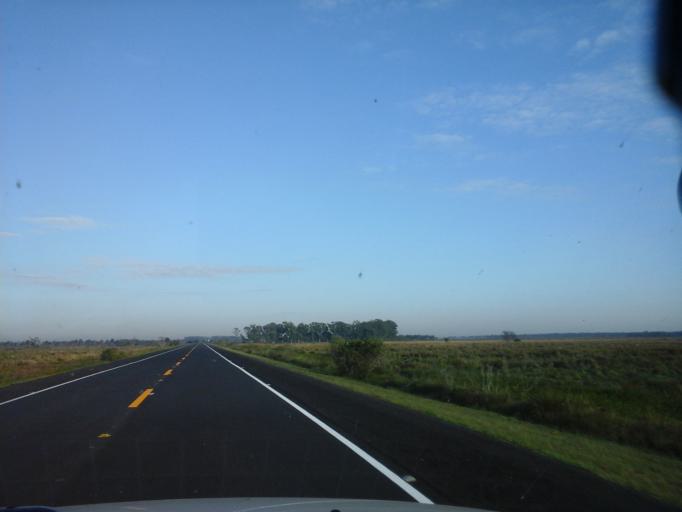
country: PY
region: Neembucu
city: Cerrito
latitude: -26.8683
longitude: -57.7967
